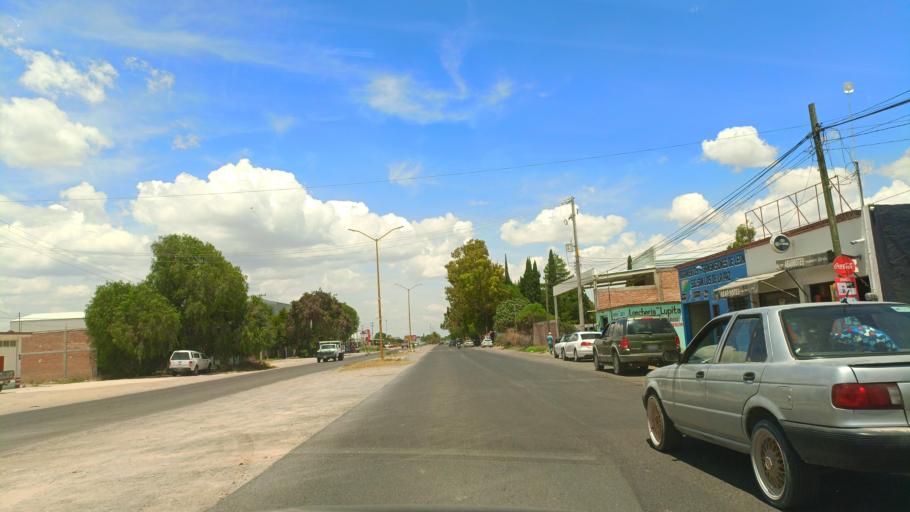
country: MX
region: Guanajuato
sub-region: San Luis de la Paz
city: San Ignacio
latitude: 21.2907
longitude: -100.5464
